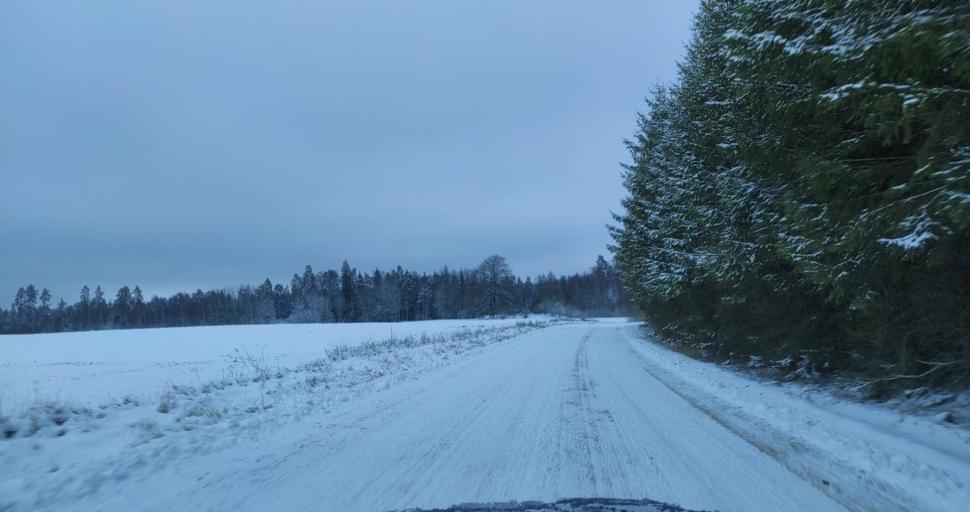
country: LV
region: Alsunga
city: Alsunga
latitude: 56.9504
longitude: 21.7542
